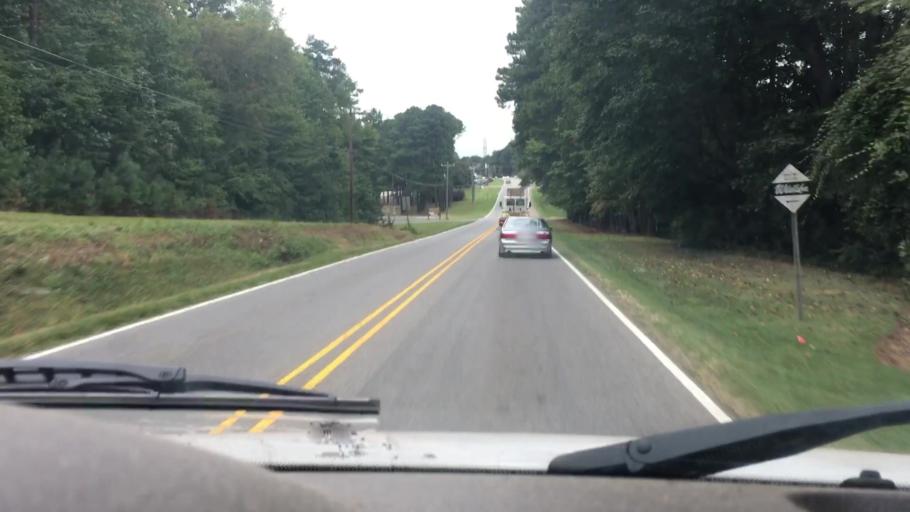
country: US
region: North Carolina
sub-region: Catawba County
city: Lake Norman of Catawba
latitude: 35.6039
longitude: -80.9268
